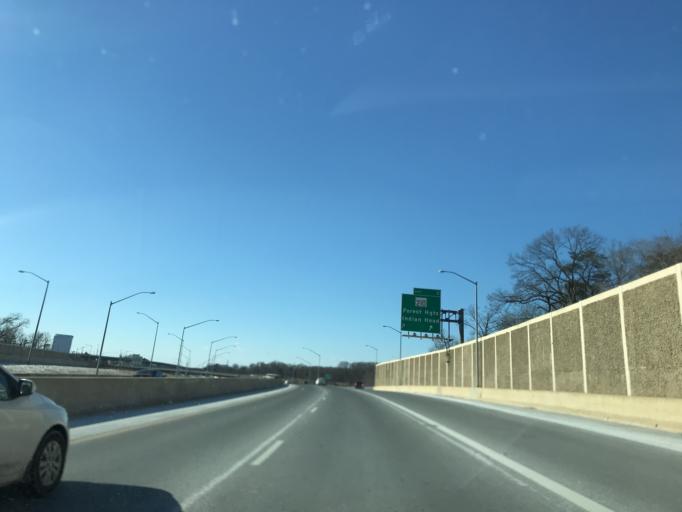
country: US
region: Maryland
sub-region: Prince George's County
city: Oxon Hill
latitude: 38.8062
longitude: -76.9925
